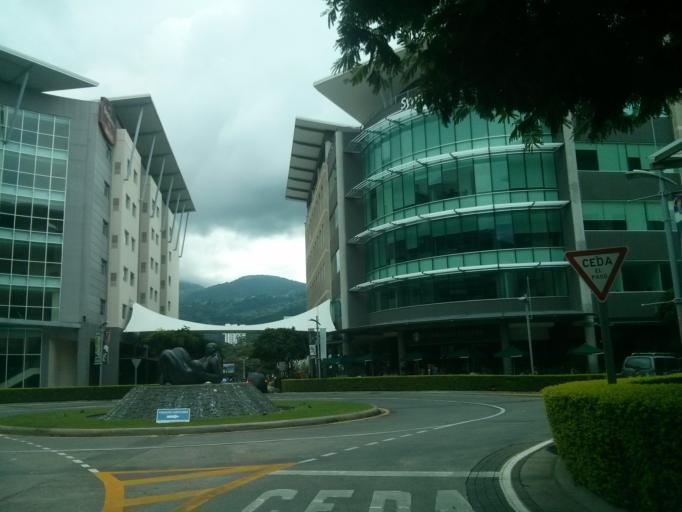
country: CR
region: San Jose
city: San Rafael
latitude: 9.9388
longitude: -84.1427
